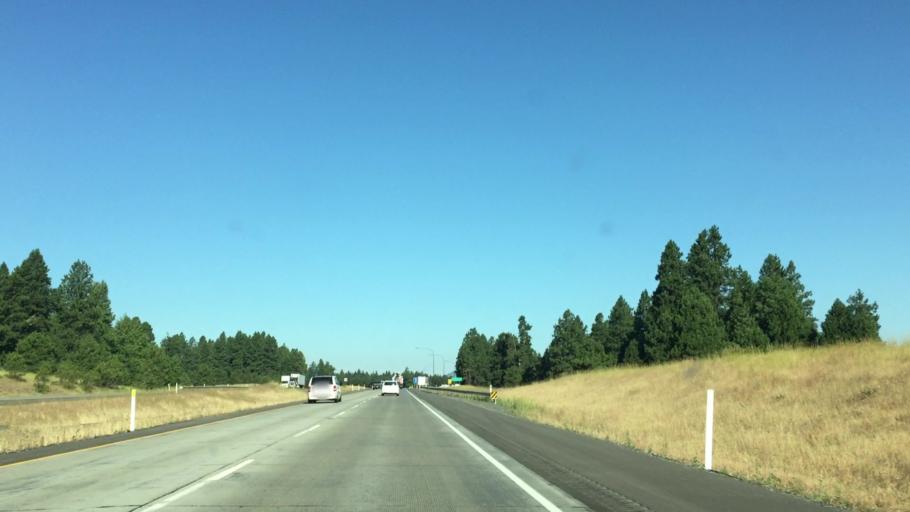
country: US
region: Washington
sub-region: Kittitas County
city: Cle Elum
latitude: 47.1591
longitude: -120.8363
